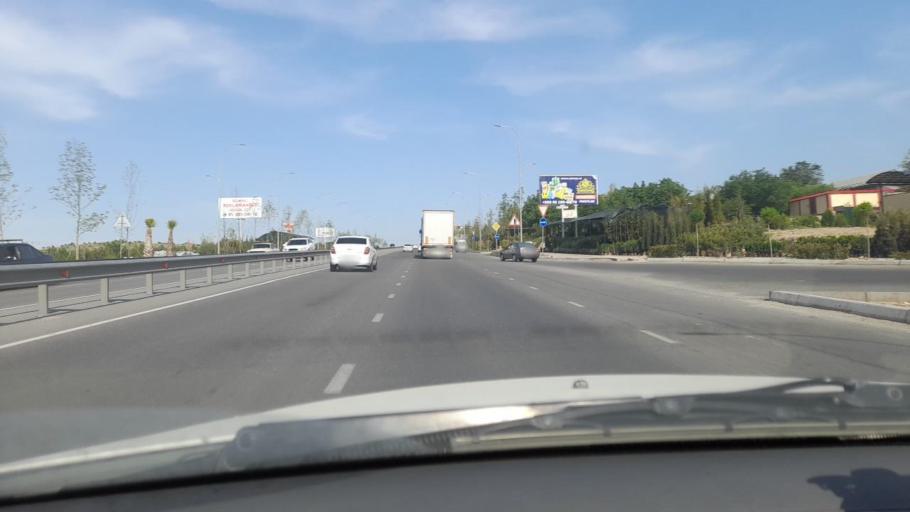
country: UZ
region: Samarqand
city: Samarqand
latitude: 39.6737
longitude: 67.0253
